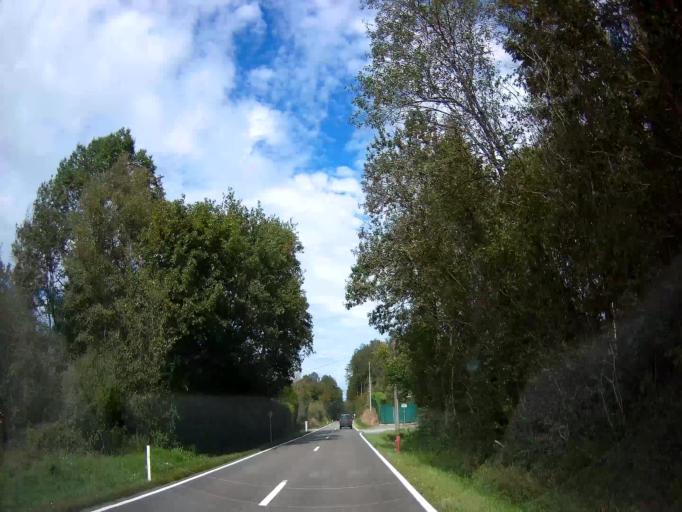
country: BE
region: Wallonia
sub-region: Province du Luxembourg
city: Hotton
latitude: 50.2990
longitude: 5.4655
